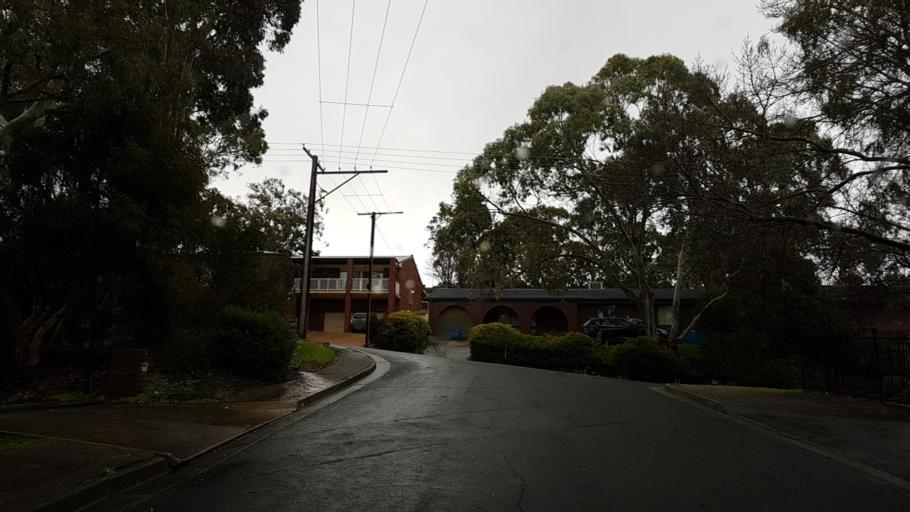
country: AU
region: South Australia
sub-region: Onkaparinga
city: Bedford Park
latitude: -35.0464
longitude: 138.5821
